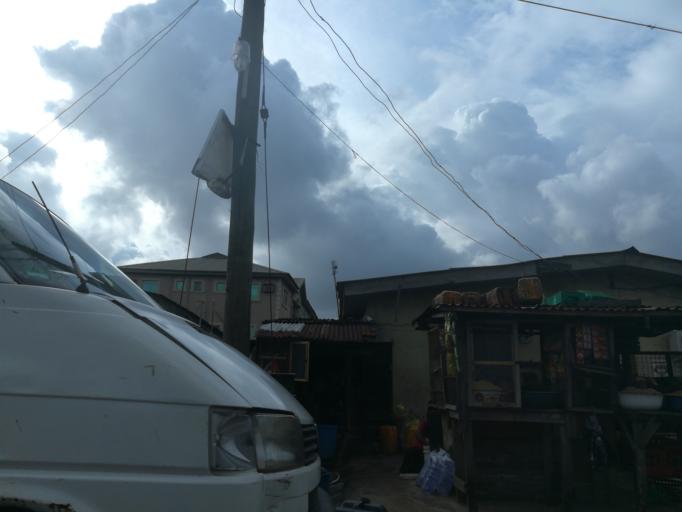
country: NG
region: Lagos
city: Somolu
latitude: 6.5430
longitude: 3.3811
